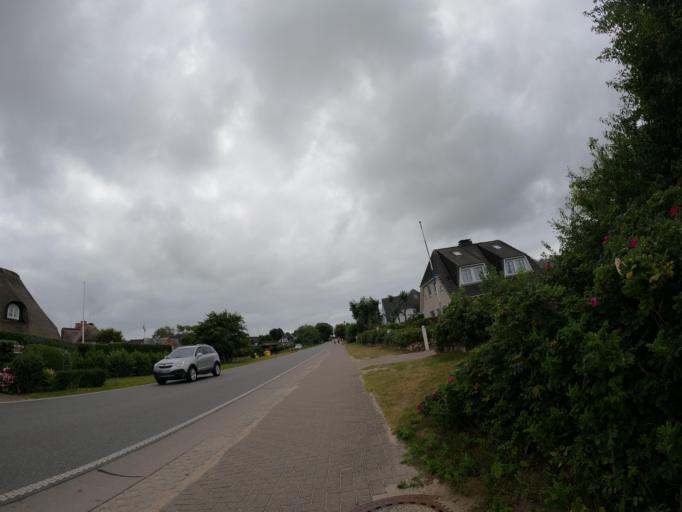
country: DE
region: Schleswig-Holstein
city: Keitum
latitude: 54.9184
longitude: 8.3582
